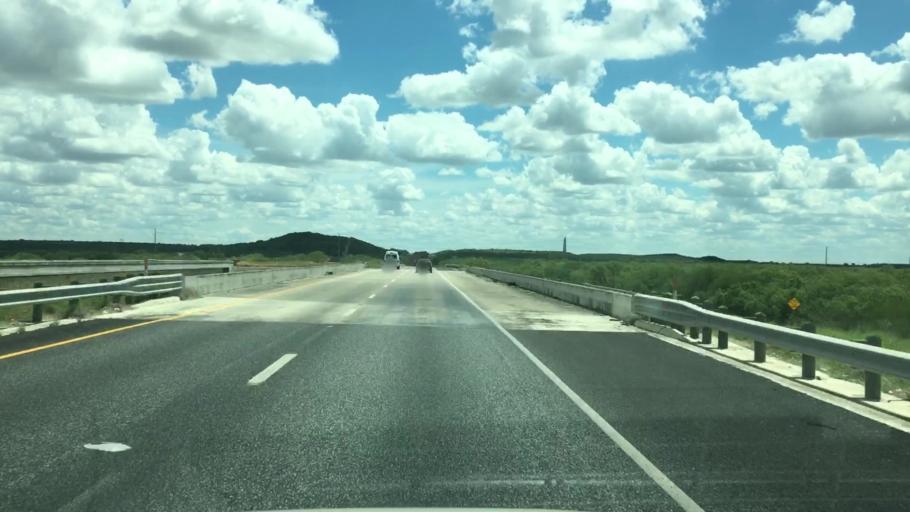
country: US
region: Texas
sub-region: Live Oak County
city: Three Rivers
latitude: 28.7340
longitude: -98.2895
